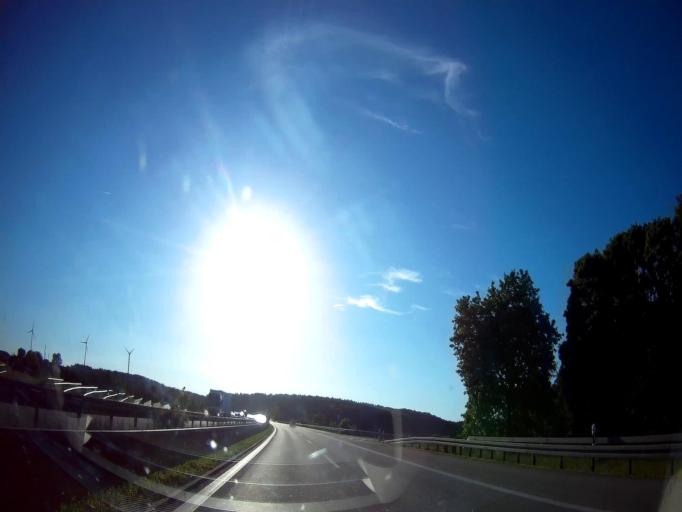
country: DE
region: Bavaria
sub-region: Upper Palatinate
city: Hohenfels
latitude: 49.1693
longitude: 11.8282
